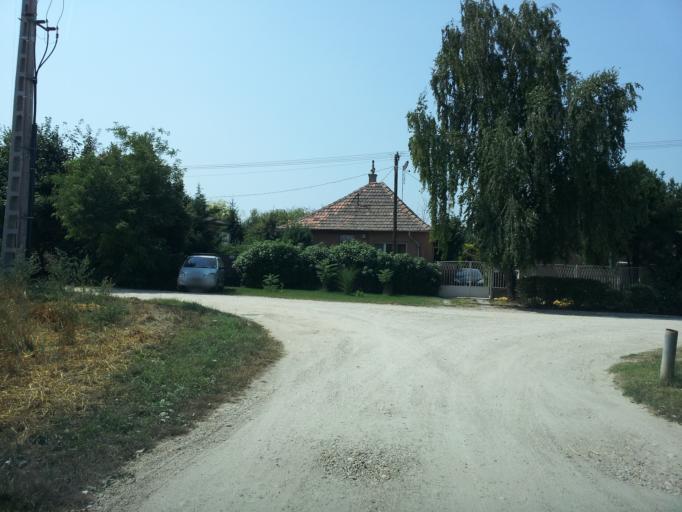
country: HU
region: Pest
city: Dunavarsany
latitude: 47.2679
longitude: 19.0730
